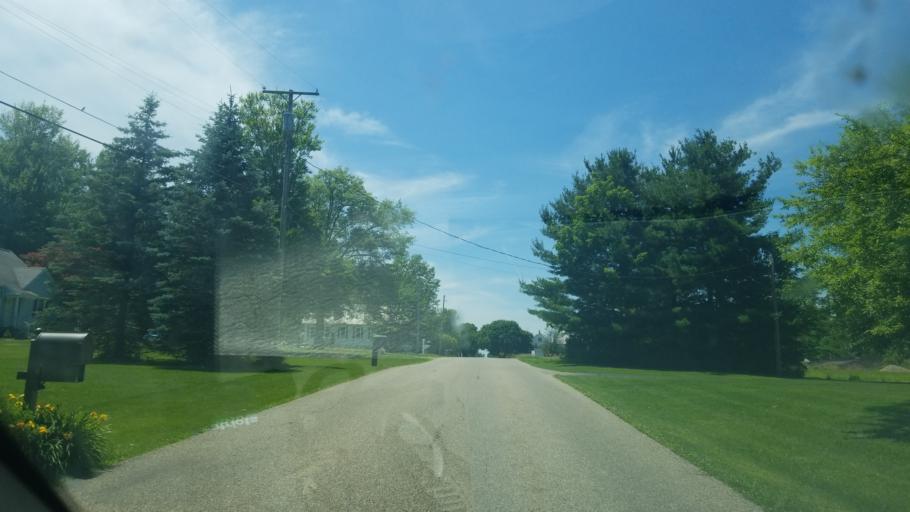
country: US
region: Ohio
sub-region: Stark County
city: Alliance
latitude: 40.8575
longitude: -81.1017
